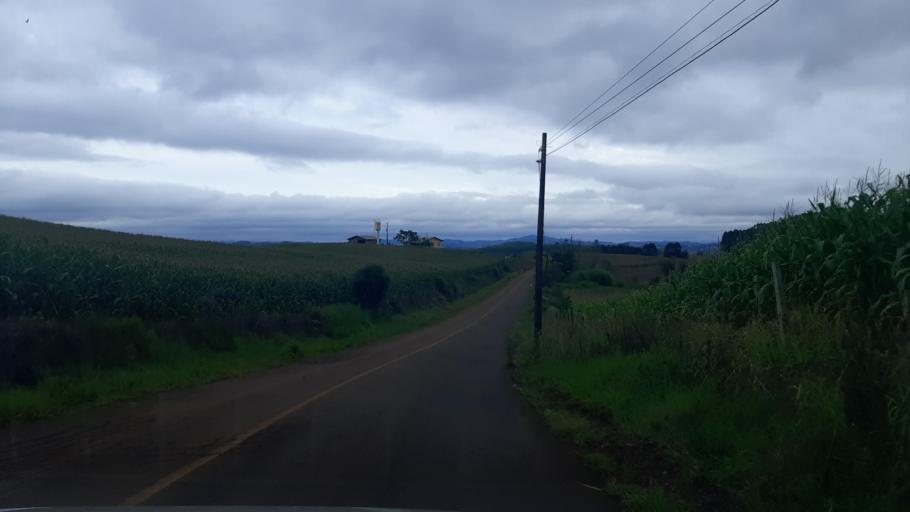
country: BR
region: Parana
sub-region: Ampere
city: Ampere
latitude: -26.0423
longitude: -53.4949
